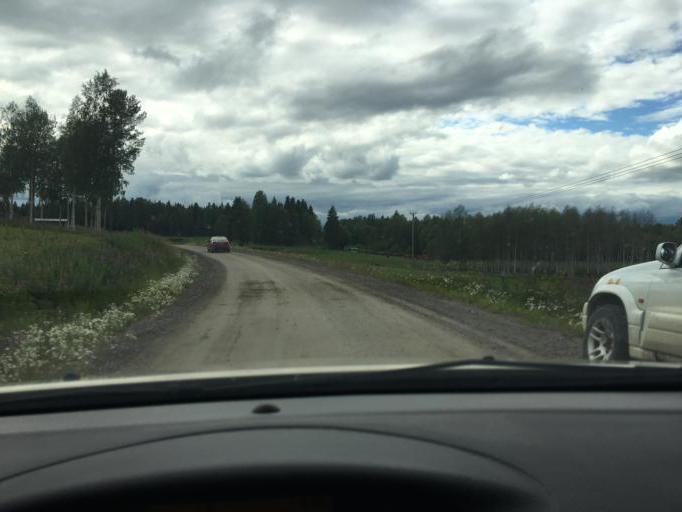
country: SE
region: Norrbotten
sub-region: Overkalix Kommun
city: OEverkalix
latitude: 66.0894
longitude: 22.8832
